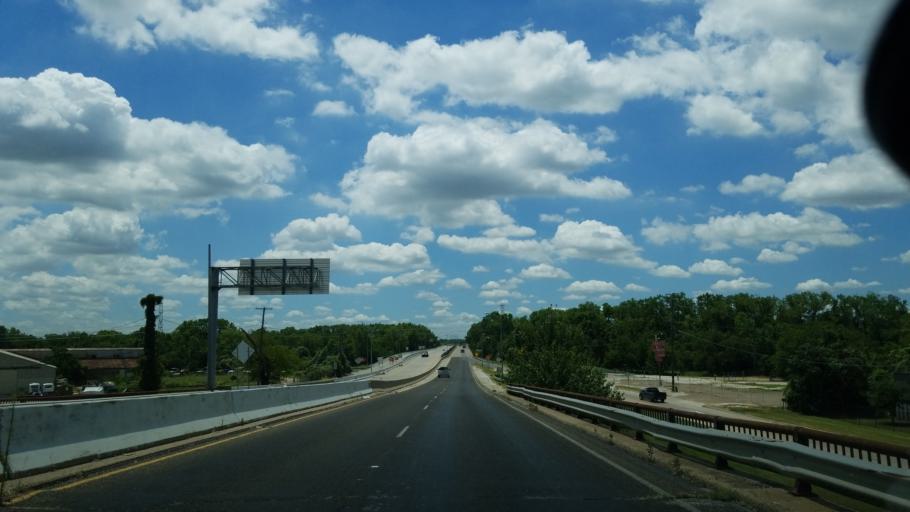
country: US
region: Texas
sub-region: Dallas County
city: Dallas
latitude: 32.7353
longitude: -96.7578
